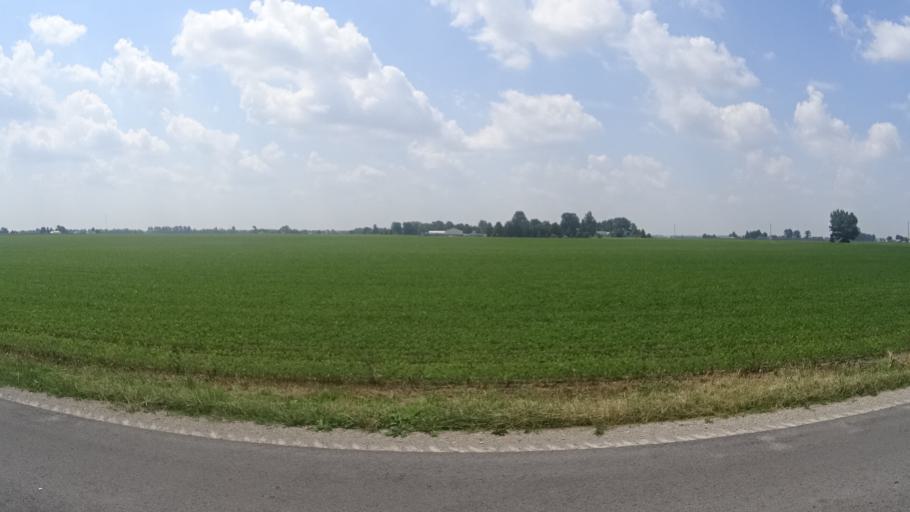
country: US
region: Ohio
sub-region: Huron County
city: Monroeville
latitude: 41.3338
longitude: -82.7181
